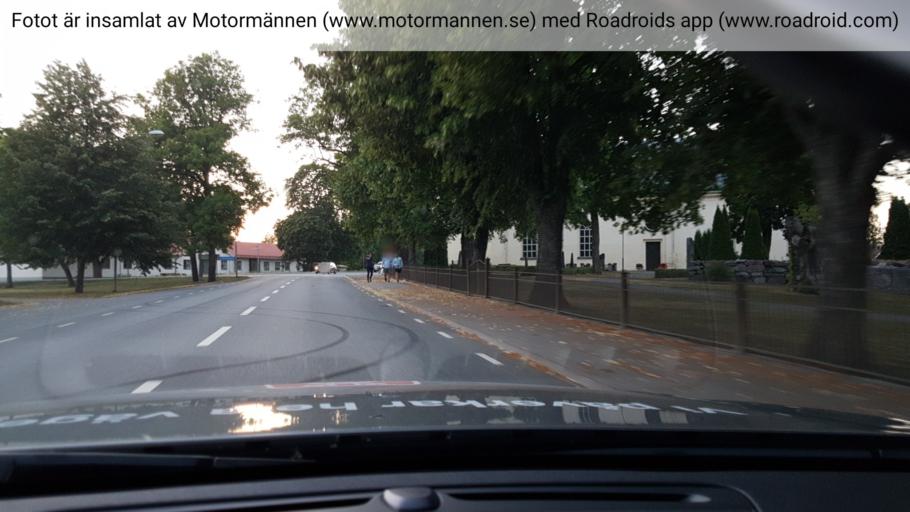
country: SE
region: Uppsala
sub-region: Heby Kommun
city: OEstervala
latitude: 60.1778
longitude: 17.1784
